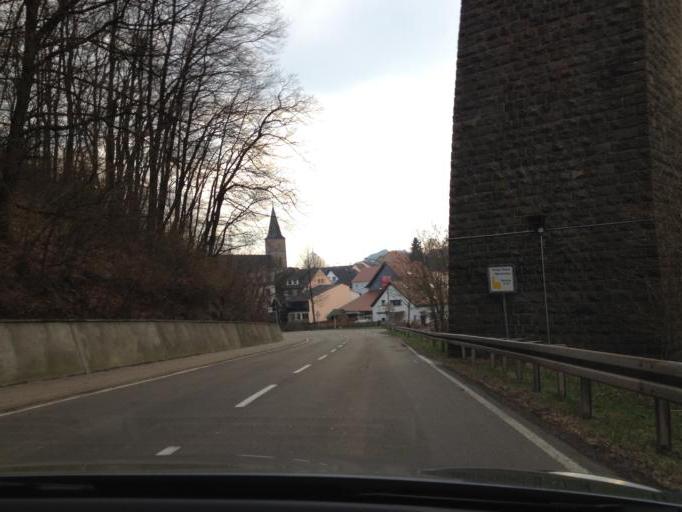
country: DE
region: Rheinland-Pfalz
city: Reichweiler
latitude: 49.5275
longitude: 7.2605
